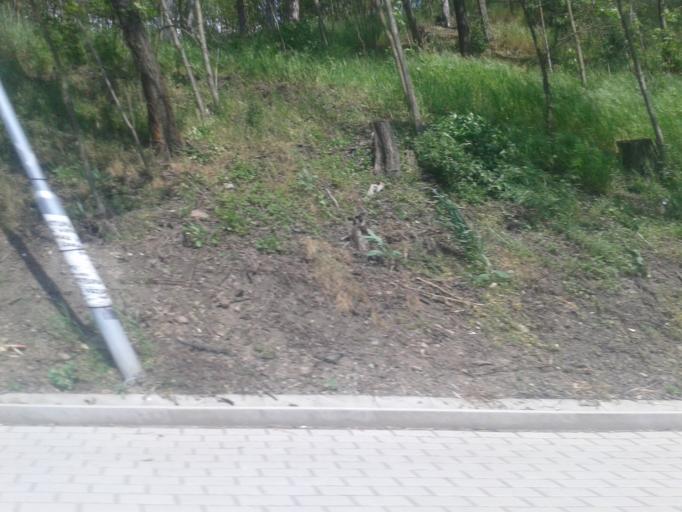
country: CZ
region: Central Bohemia
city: Zdice
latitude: 49.9166
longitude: 13.9842
